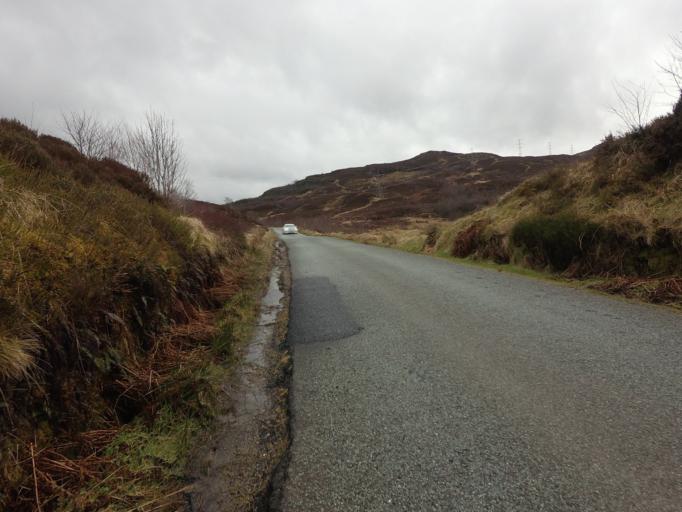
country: GB
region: Scotland
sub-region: West Dunbartonshire
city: Balloch
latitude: 56.2463
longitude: -4.5844
